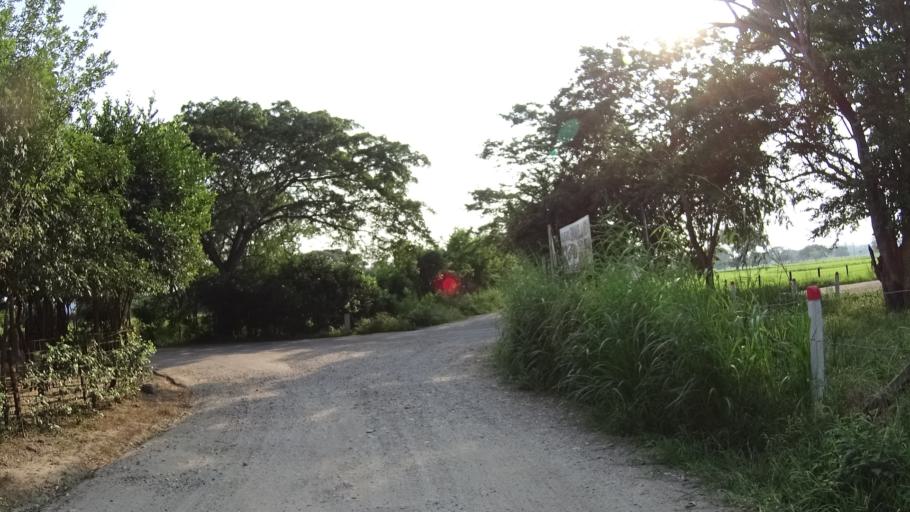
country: CO
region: Cundinamarca
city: Puerto Salgar
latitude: 5.5098
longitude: -74.6905
